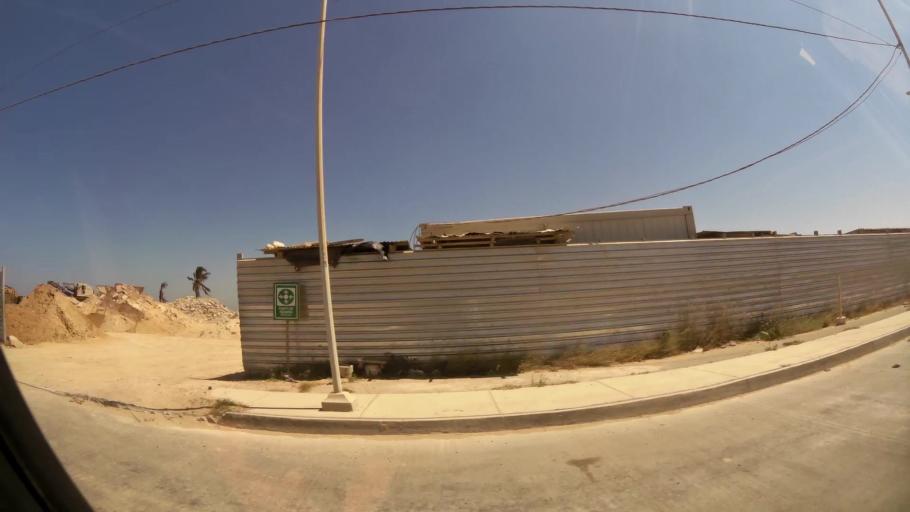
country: CO
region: Atlantico
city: Barranquilla
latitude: 10.9933
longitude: -74.7702
